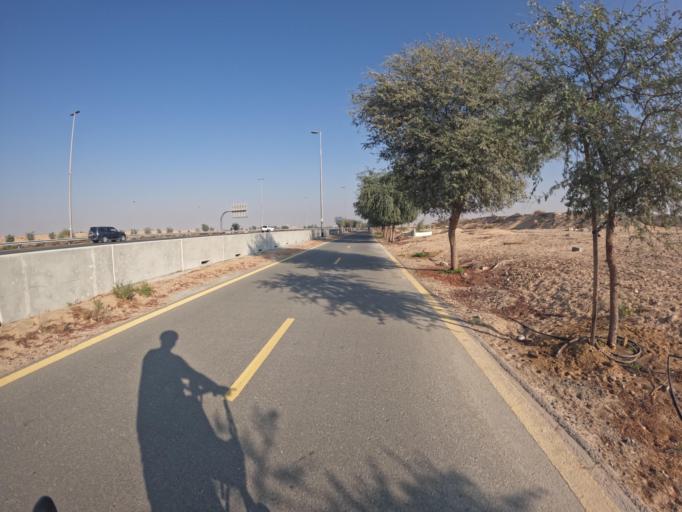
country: AE
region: Dubai
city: Dubai
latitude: 24.9553
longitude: 55.3428
